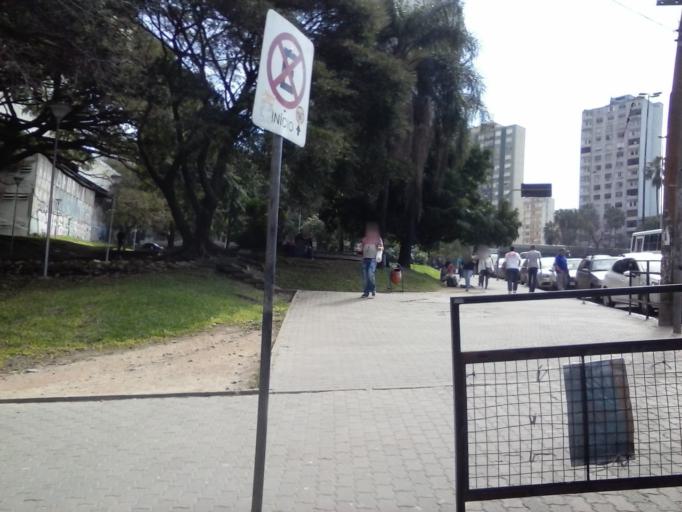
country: BR
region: Rio Grande do Sul
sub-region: Porto Alegre
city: Porto Alegre
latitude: -30.0323
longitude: -51.2233
